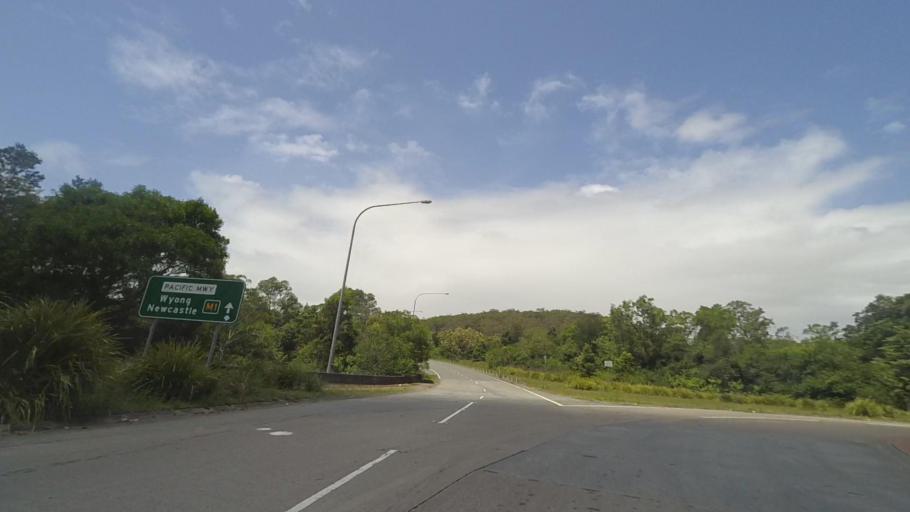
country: AU
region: New South Wales
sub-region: Gosford Shire
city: Lisarow
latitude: -33.3440
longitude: 151.3684
